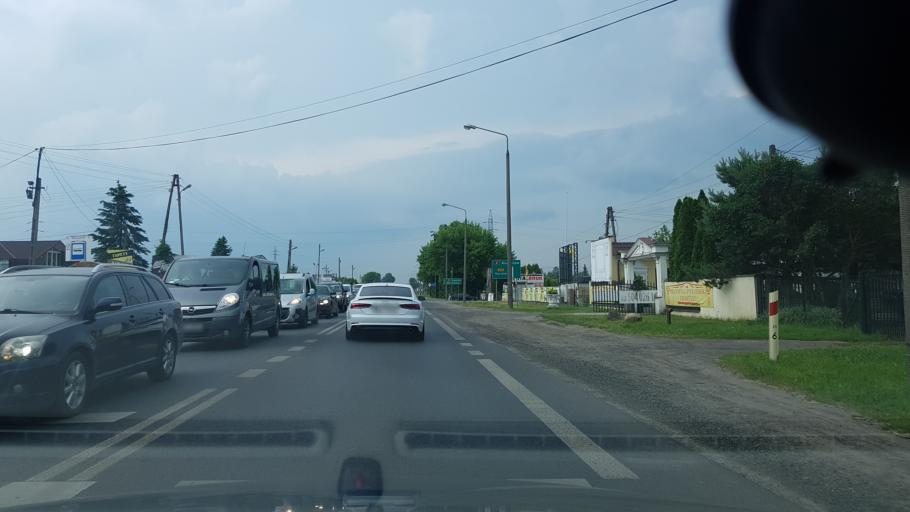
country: PL
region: Masovian Voivodeship
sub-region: Powiat legionowski
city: Michalow-Reginow
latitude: 52.4156
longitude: 20.9643
